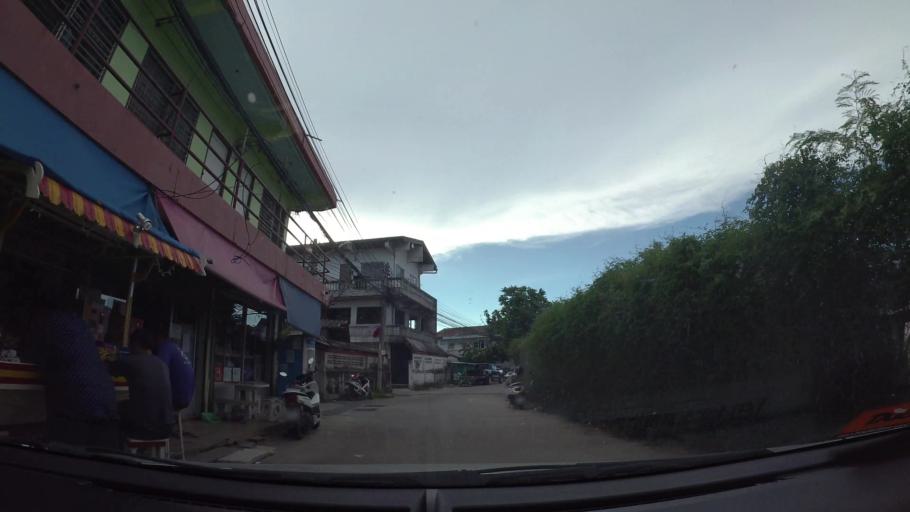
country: TH
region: Chon Buri
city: Phatthaya
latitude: 12.9177
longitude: 100.8754
